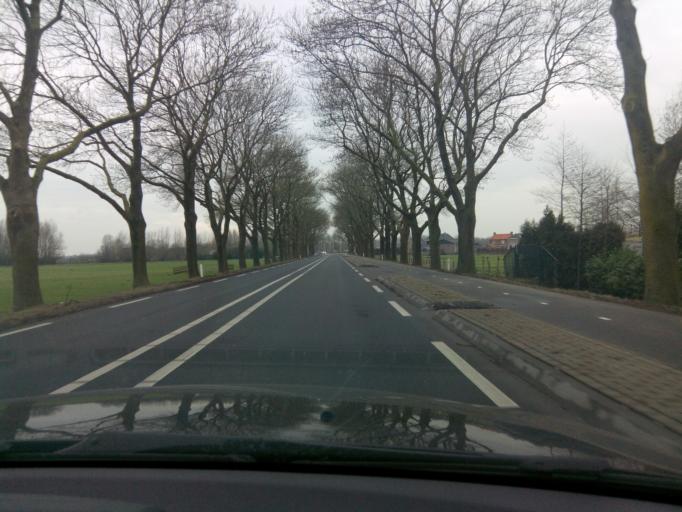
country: NL
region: South Holland
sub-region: Gemeente Leerdam
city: Leerdam
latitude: 51.9391
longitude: 5.1381
